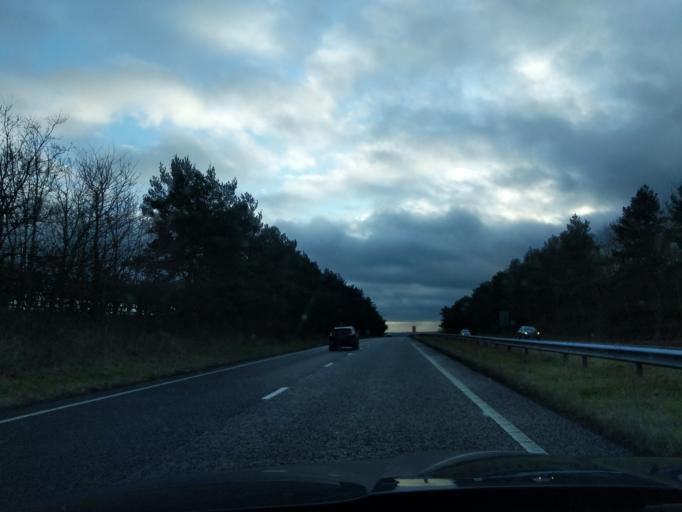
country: GB
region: England
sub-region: Northumberland
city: Felton
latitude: 55.3213
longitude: -1.7246
